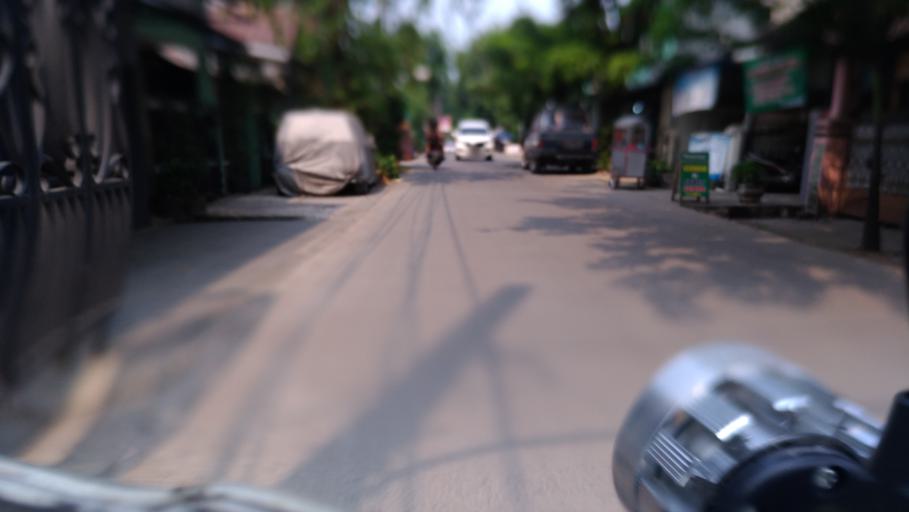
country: ID
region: West Java
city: Depok
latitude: -6.3619
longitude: 106.8732
